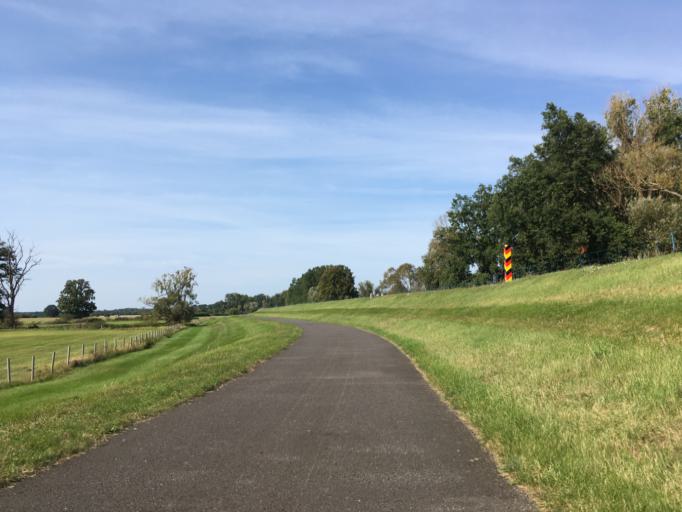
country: DE
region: Brandenburg
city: Vogelsang
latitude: 52.2304
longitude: 14.7054
